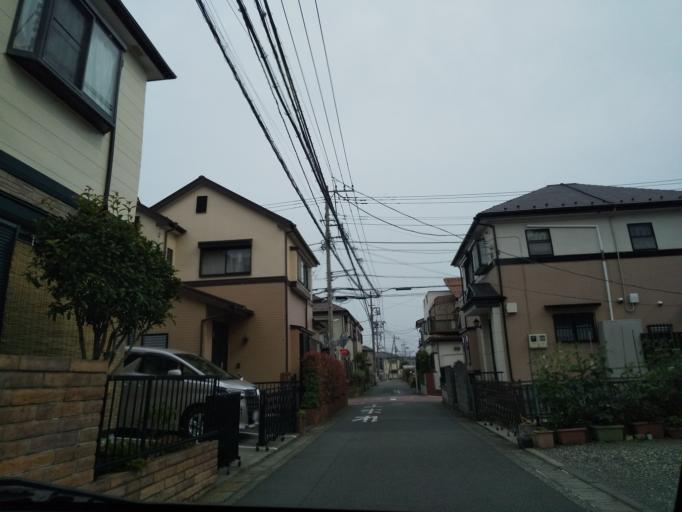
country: JP
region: Kanagawa
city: Minami-rinkan
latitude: 35.4642
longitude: 139.4266
